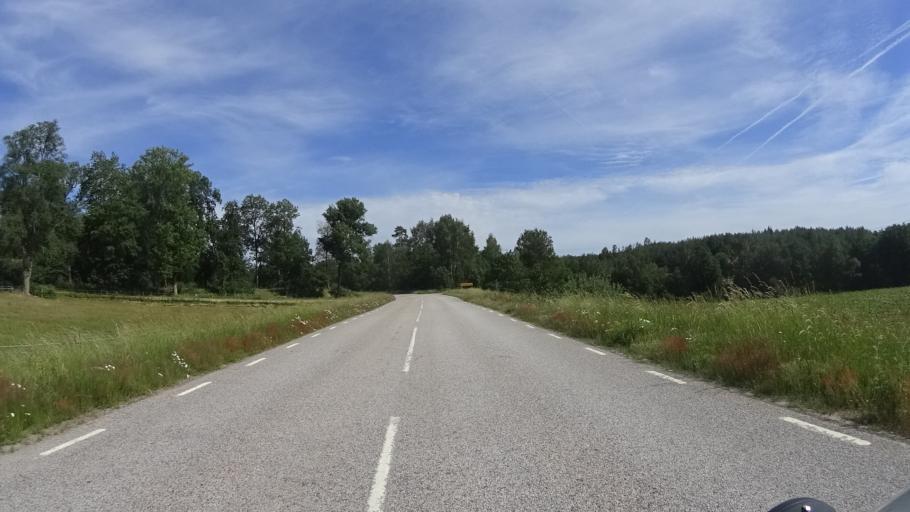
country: SE
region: Kalmar
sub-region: Vasterviks Kommun
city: Overum
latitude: 57.9051
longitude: 16.1755
